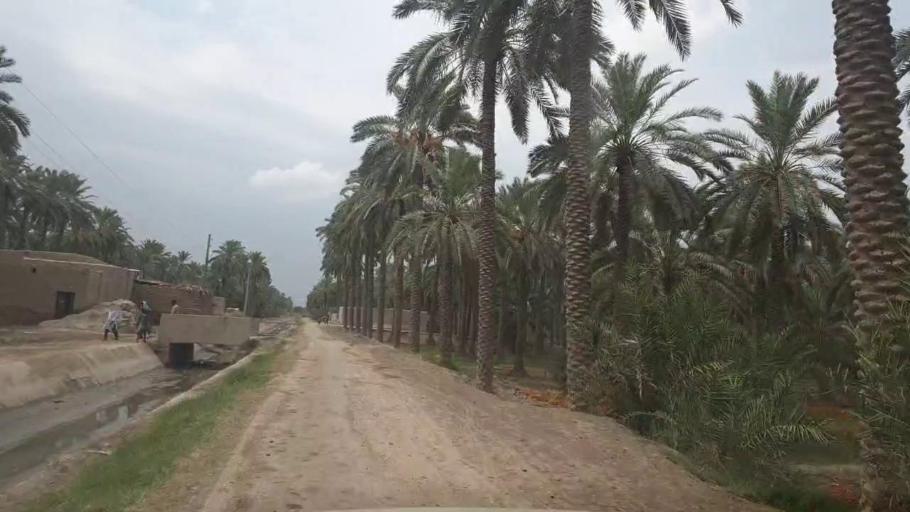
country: PK
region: Sindh
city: Khairpur
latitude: 27.6110
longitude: 68.8042
